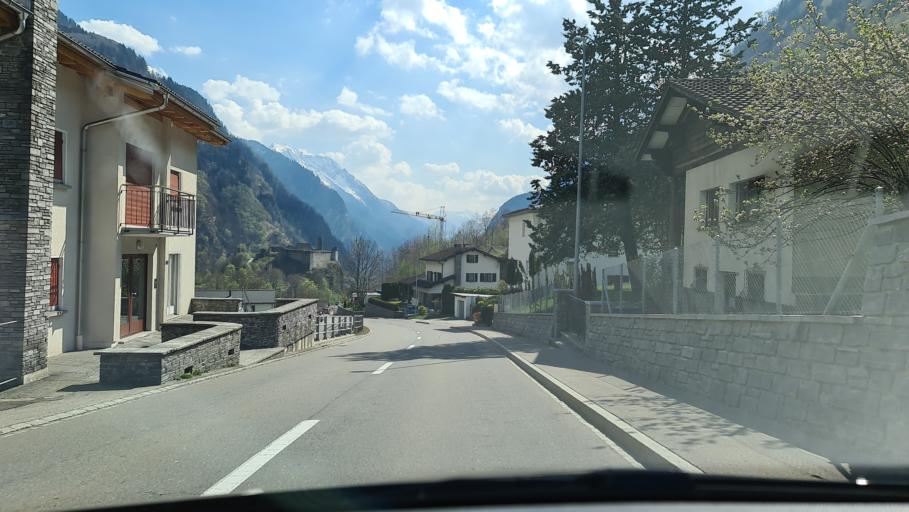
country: CH
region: Grisons
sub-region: Moesa District
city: Mesocco
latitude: 46.3871
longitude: 9.2335
